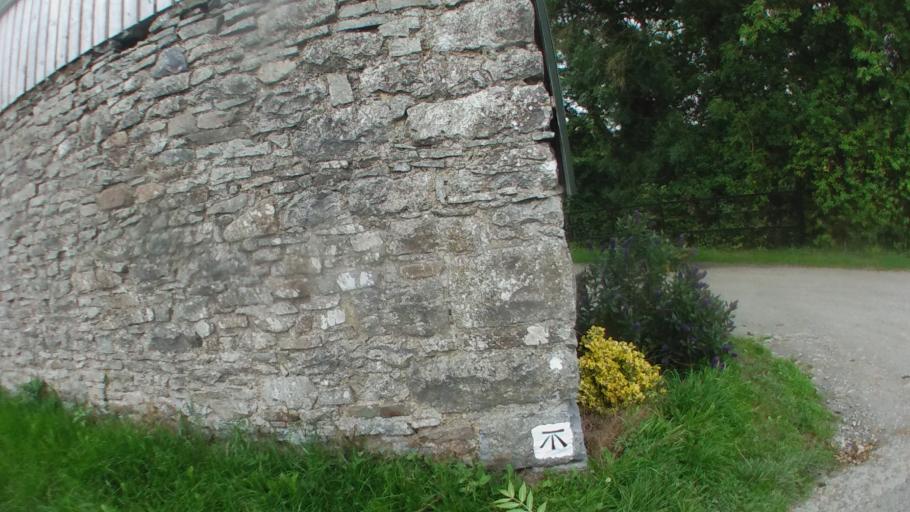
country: IE
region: Leinster
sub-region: Kilkenny
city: Kilkenny
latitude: 52.7085
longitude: -7.1944
